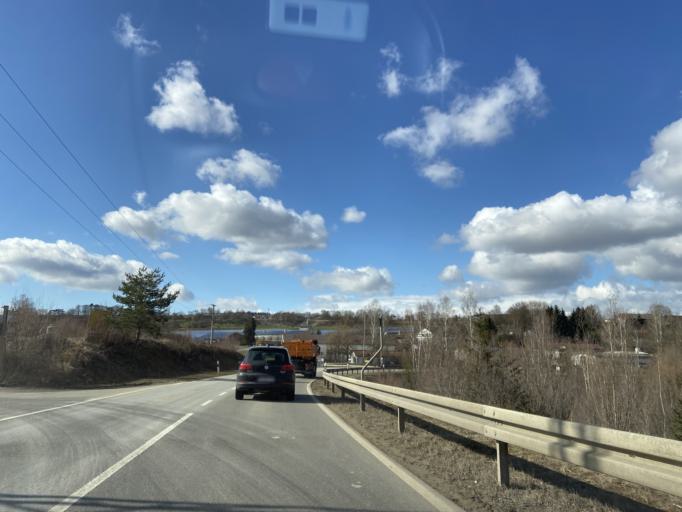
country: DE
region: Baden-Wuerttemberg
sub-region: Tuebingen Region
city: Inzigkofen
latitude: 48.0643
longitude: 9.1821
